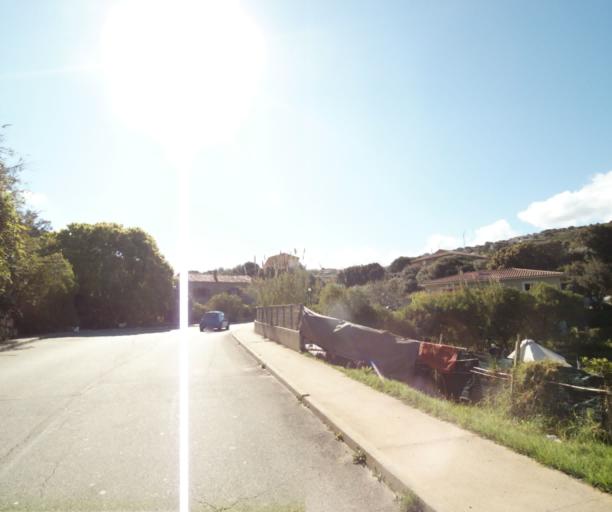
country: FR
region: Corsica
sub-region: Departement de la Corse-du-Sud
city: Propriano
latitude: 41.6726
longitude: 8.9049
